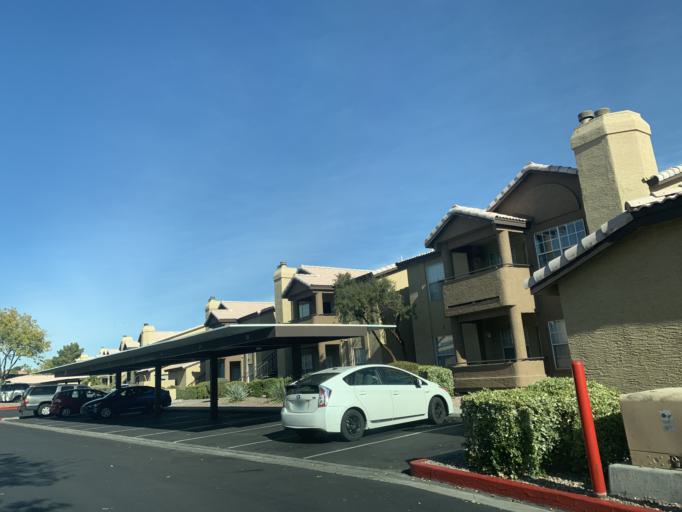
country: US
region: Nevada
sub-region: Clark County
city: Summerlin South
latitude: 36.1280
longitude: -115.2907
